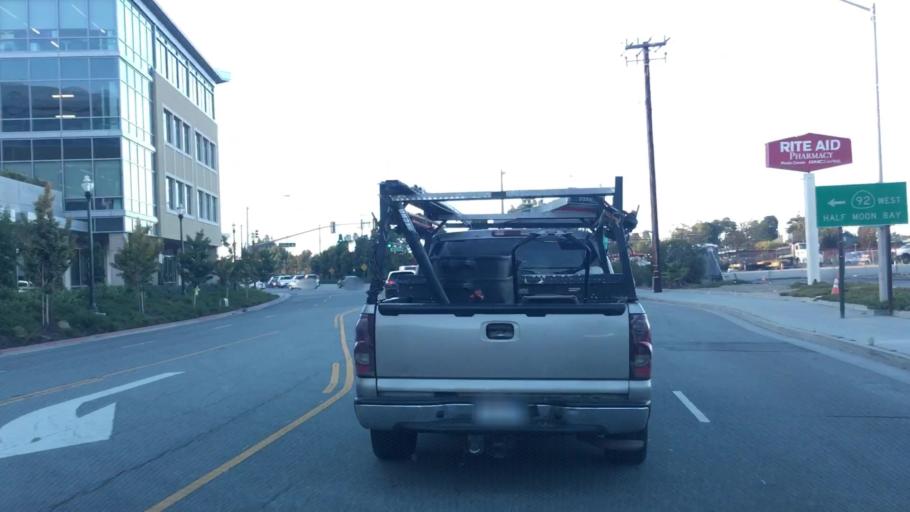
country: US
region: California
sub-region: San Mateo County
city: San Mateo
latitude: 37.5534
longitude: -122.3055
